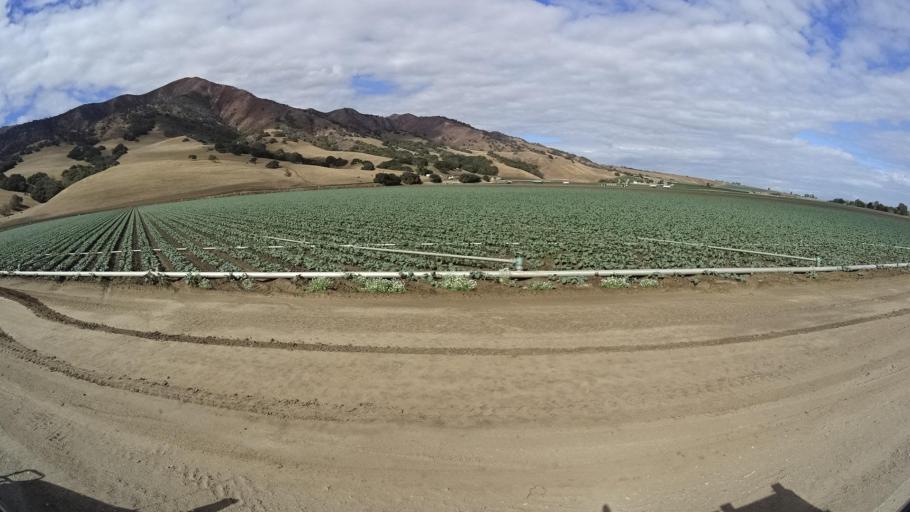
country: US
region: California
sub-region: Monterey County
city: Chualar
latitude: 36.5376
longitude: -121.5396
